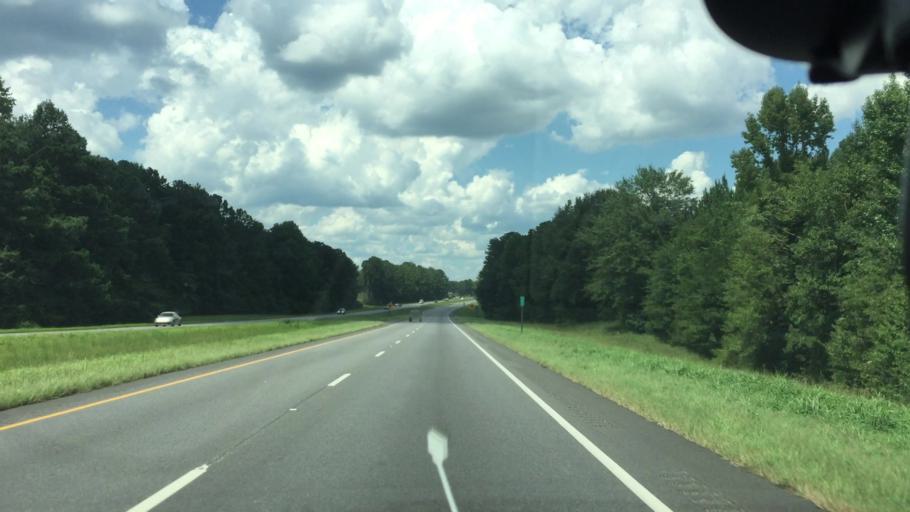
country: US
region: Alabama
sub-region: Pike County
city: Troy
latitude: 31.8868
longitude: -86.0071
